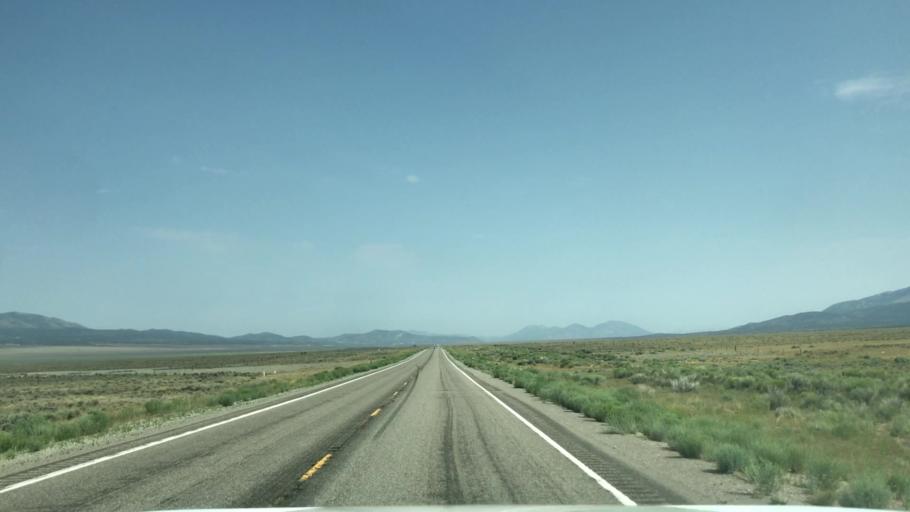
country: US
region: Nevada
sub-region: White Pine County
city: Ely
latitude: 39.0653
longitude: -114.7354
